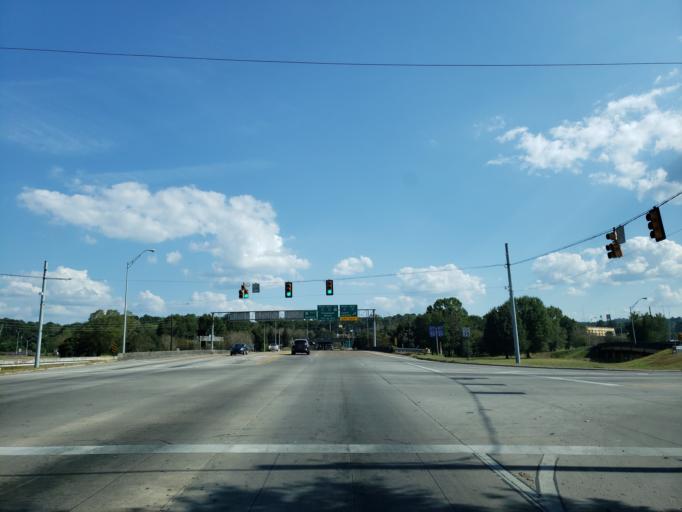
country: US
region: Mississippi
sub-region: Lauderdale County
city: Meridian
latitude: 32.3559
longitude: -88.6931
